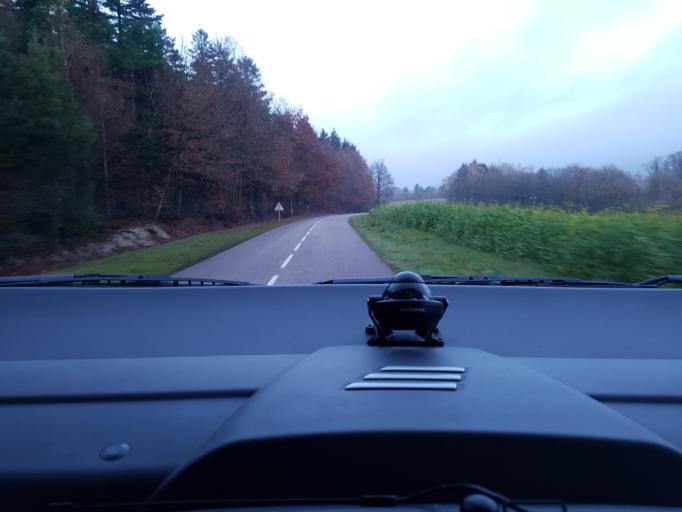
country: FR
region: Lower Normandy
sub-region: Departement de l'Orne
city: Tourouvre
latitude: 48.6012
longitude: 0.6780
